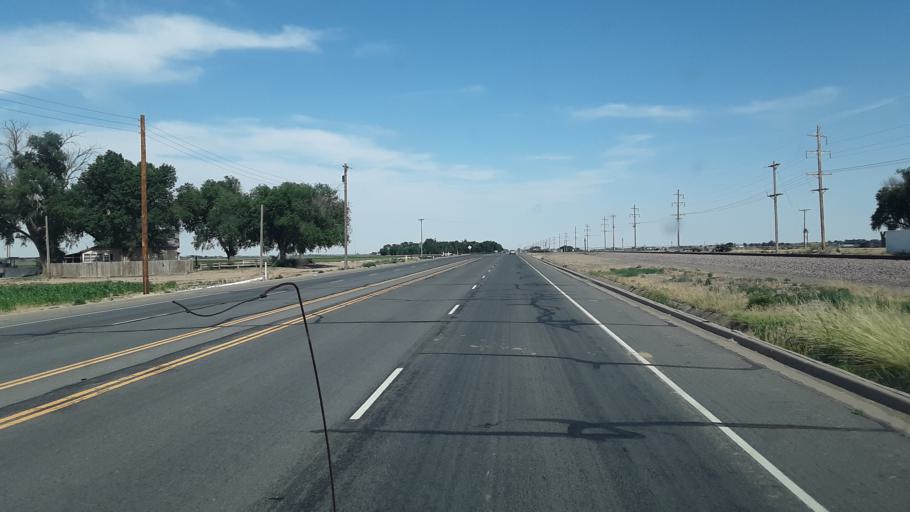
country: US
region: Colorado
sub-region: Otero County
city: Rocky Ford
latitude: 38.0944
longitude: -103.8227
